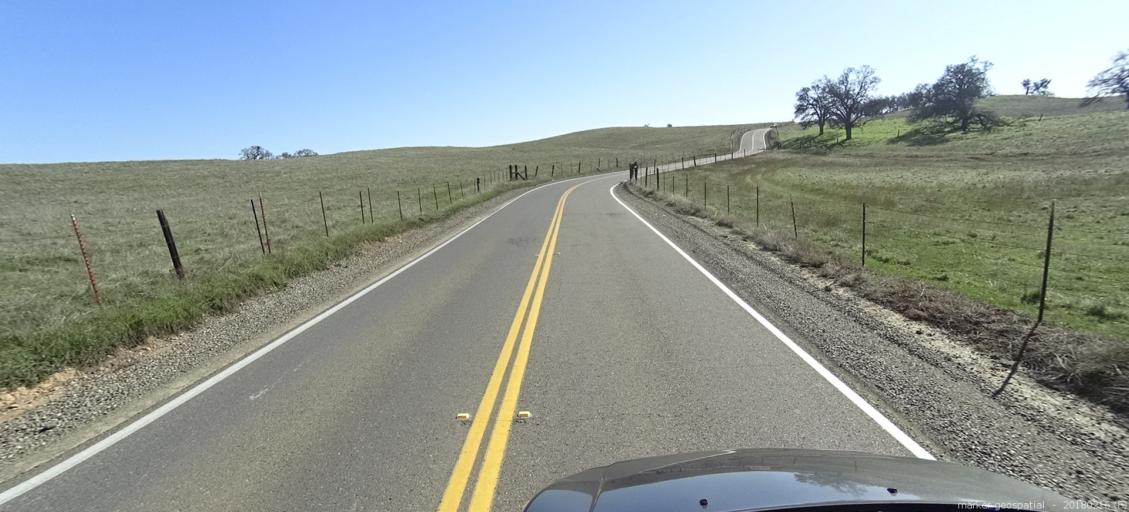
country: US
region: California
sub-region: Sacramento County
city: Rancho Murieta
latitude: 38.5774
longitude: -121.1294
